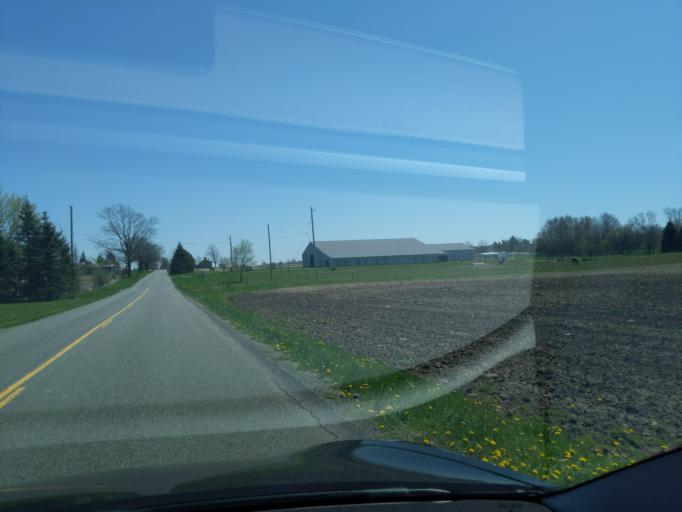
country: US
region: Michigan
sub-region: Ingham County
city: Holt
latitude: 42.5531
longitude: -84.5284
